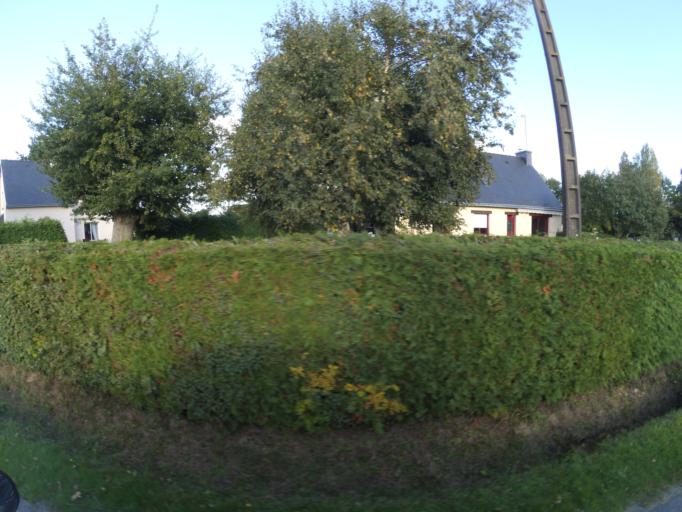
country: FR
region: Brittany
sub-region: Departement du Morbihan
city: Saint-Vincent-sur-Oust
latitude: 47.7147
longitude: -2.1734
